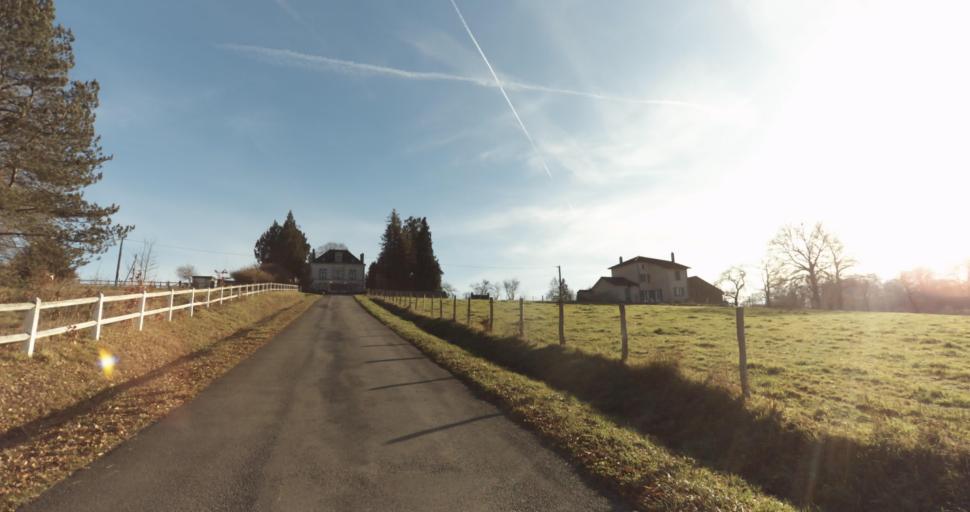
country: FR
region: Limousin
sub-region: Departement de la Haute-Vienne
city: Saint-Priest-sous-Aixe
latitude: 45.7995
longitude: 1.1098
